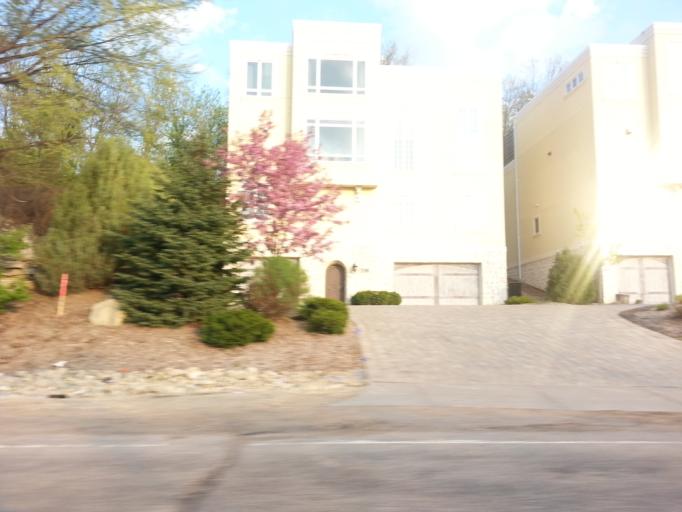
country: US
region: Minnesota
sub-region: Dakota County
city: Mendota Heights
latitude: 44.8924
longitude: -93.1522
